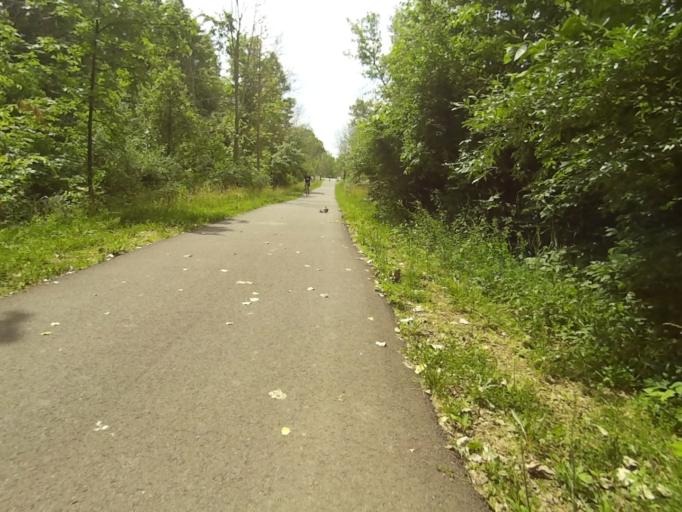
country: US
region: Ohio
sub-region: Summit County
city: Boston Heights
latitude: 41.2558
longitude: -81.5190
